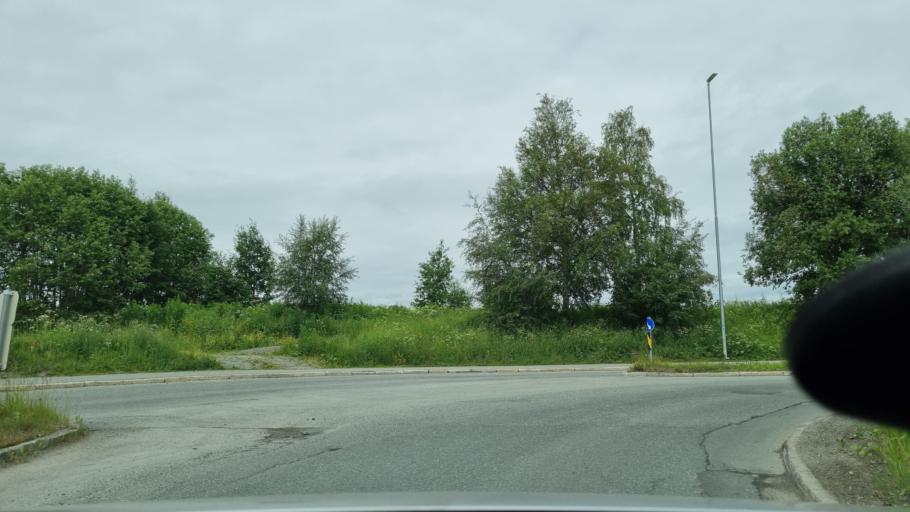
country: NO
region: Sor-Trondelag
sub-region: Melhus
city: Melhus
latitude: 63.3479
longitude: 10.3300
